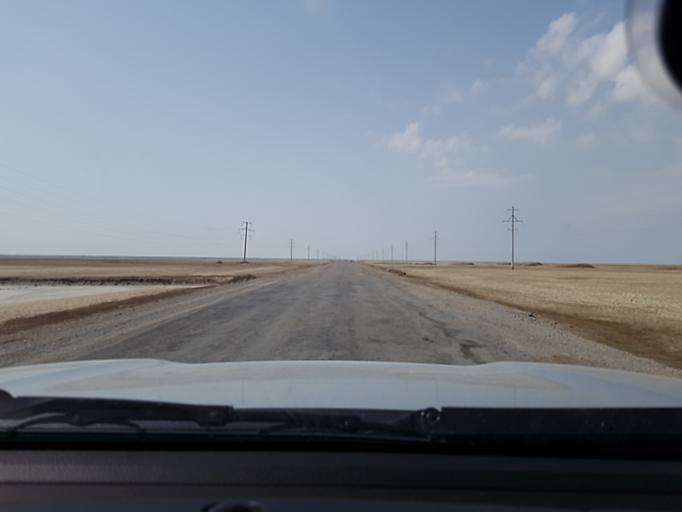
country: TM
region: Balkan
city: Gumdag
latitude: 39.0773
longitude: 54.5843
